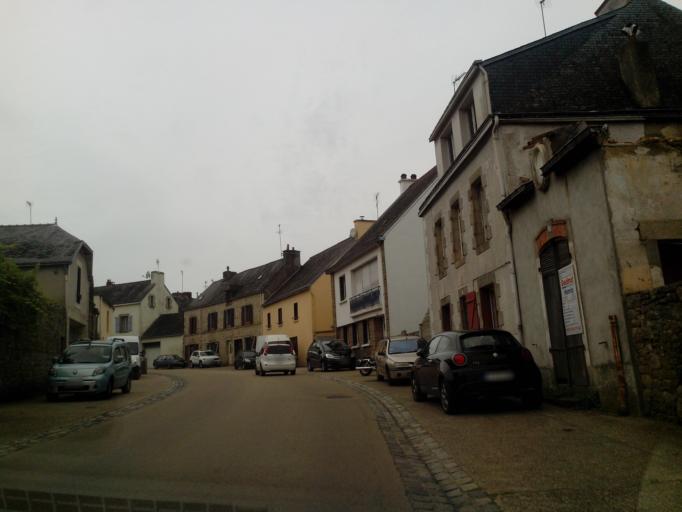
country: FR
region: Brittany
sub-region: Departement du Morbihan
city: Pont-Scorff
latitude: 47.8360
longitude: -3.3980
